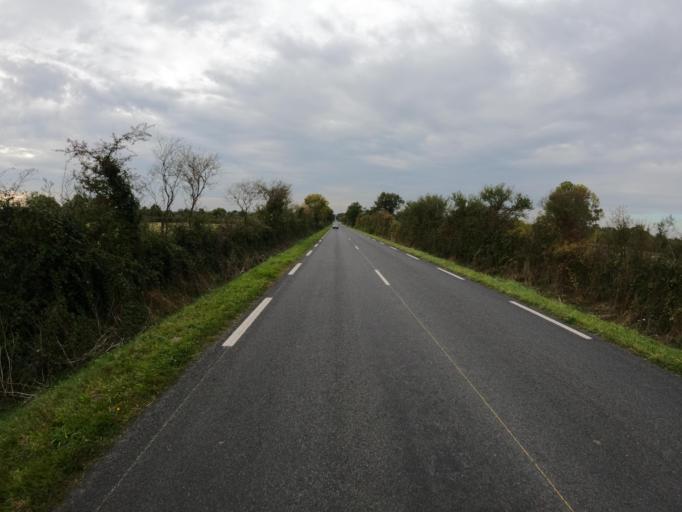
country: FR
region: Pays de la Loire
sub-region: Departement de la Loire-Atlantique
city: Getigne
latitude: 47.0702
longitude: -1.2153
